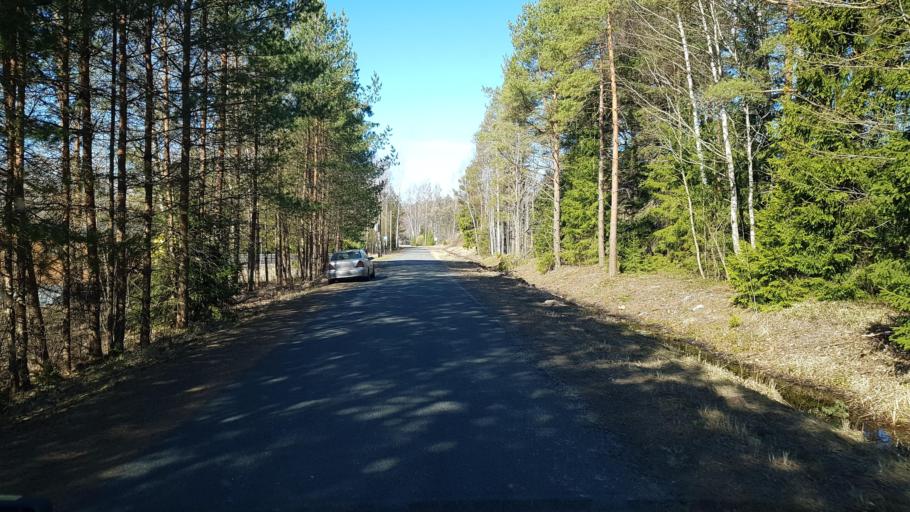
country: EE
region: Paernumaa
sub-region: Audru vald
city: Audru
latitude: 58.4246
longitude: 24.3572
